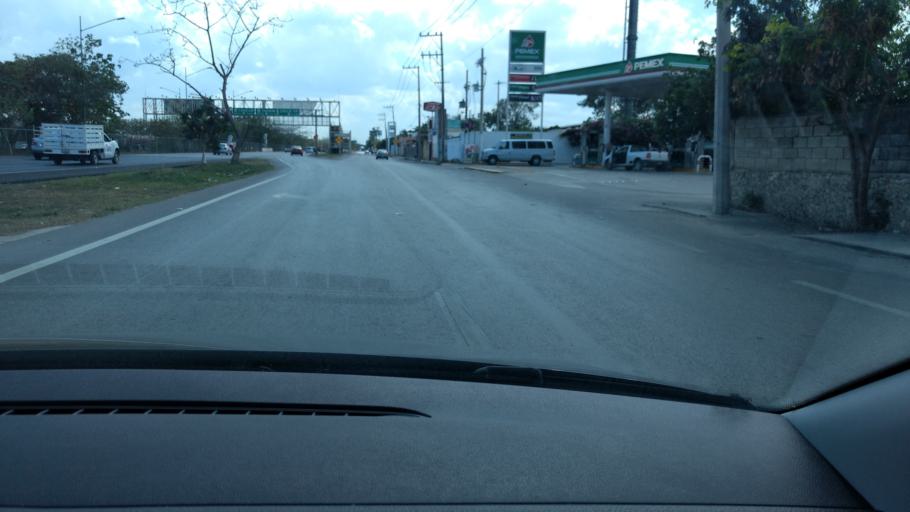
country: MX
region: Yucatan
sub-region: Kanasin
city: Kanasin
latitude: 20.9762
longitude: -89.5649
